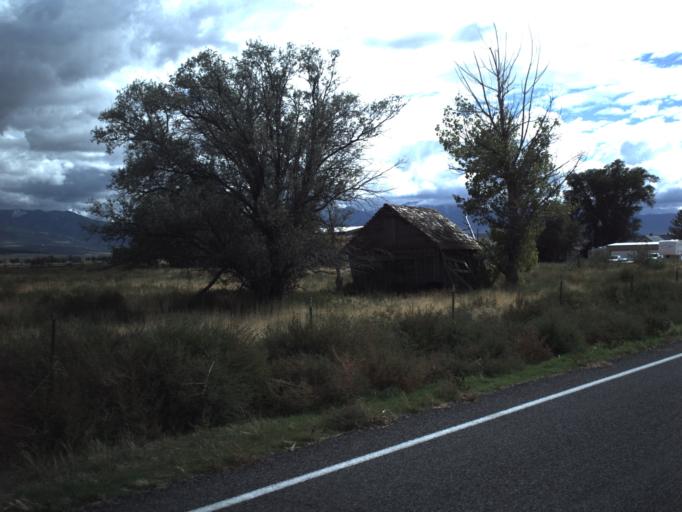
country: US
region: Utah
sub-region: Millard County
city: Fillmore
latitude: 39.0602
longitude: -112.4098
